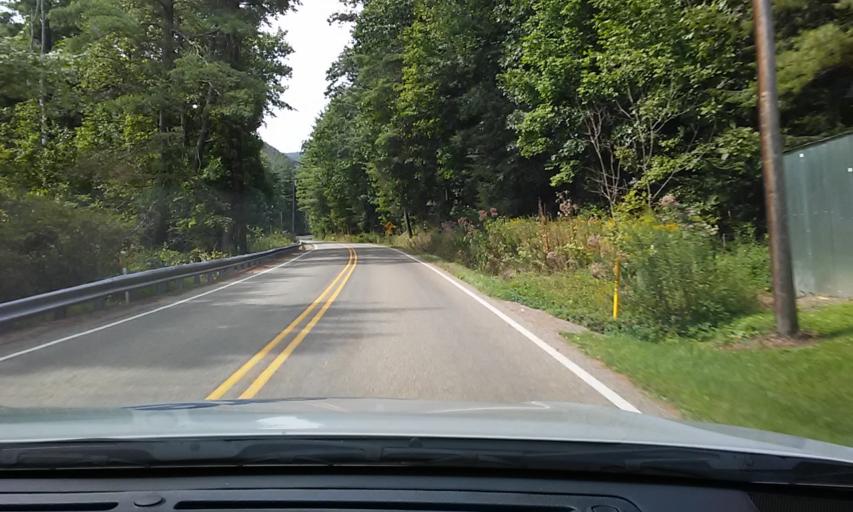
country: US
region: Pennsylvania
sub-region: Cameron County
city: Emporium
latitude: 41.3348
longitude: -78.3204
